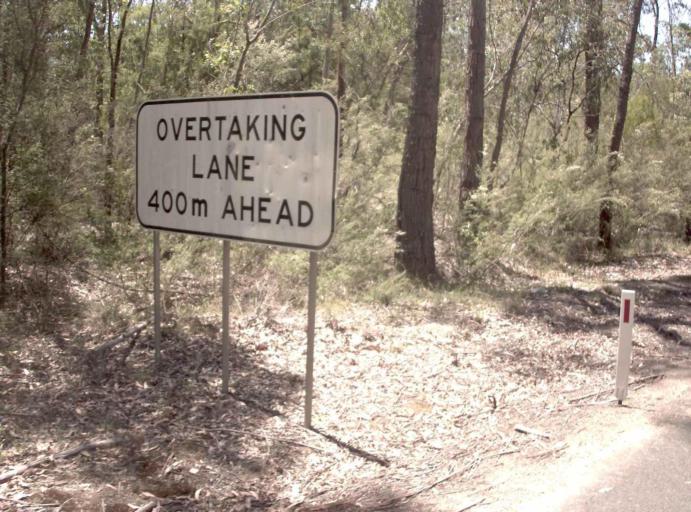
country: AU
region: Victoria
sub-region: East Gippsland
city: Lakes Entrance
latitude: -37.7325
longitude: 148.1057
